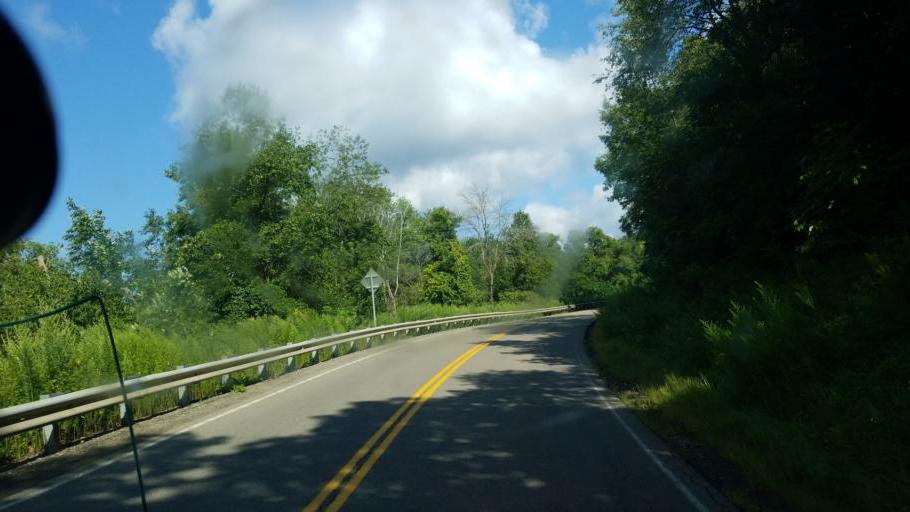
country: US
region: New York
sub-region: Steuben County
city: Canisteo
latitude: 42.2734
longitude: -77.5959
